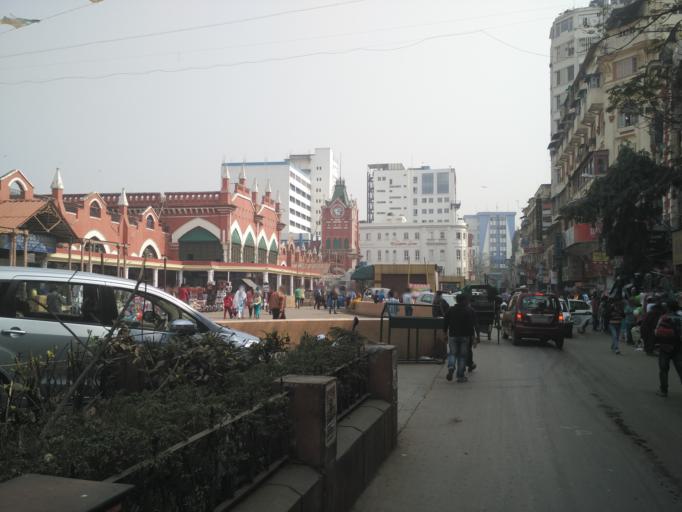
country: IN
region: West Bengal
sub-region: Kolkata
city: Bara Bazar
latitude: 22.5594
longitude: 88.3522
